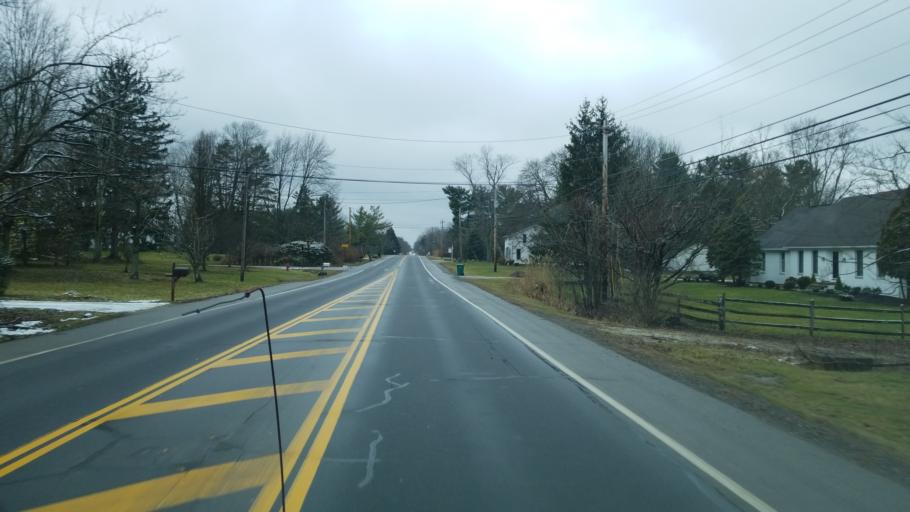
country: US
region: Ohio
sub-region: Summit County
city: Hudson
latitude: 41.2398
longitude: -81.3951
